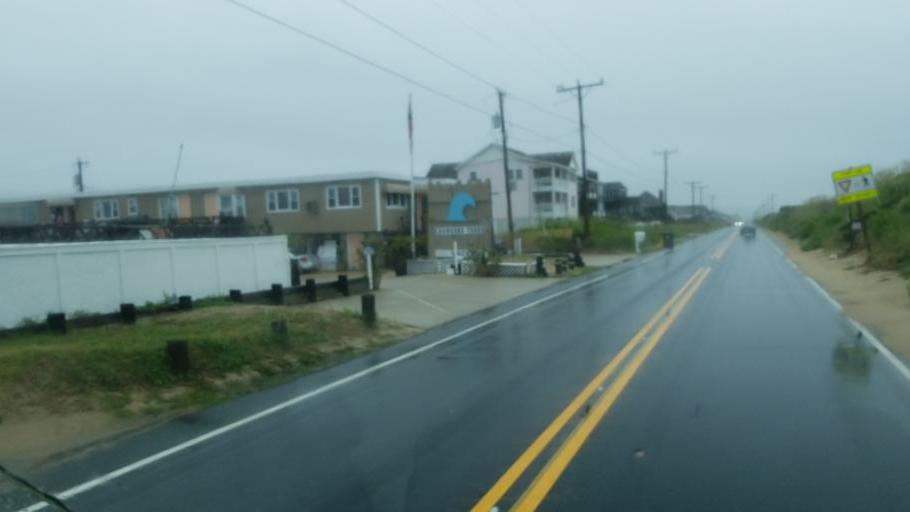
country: US
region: North Carolina
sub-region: Dare County
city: Kitty Hawk
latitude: 36.0564
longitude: -75.6834
